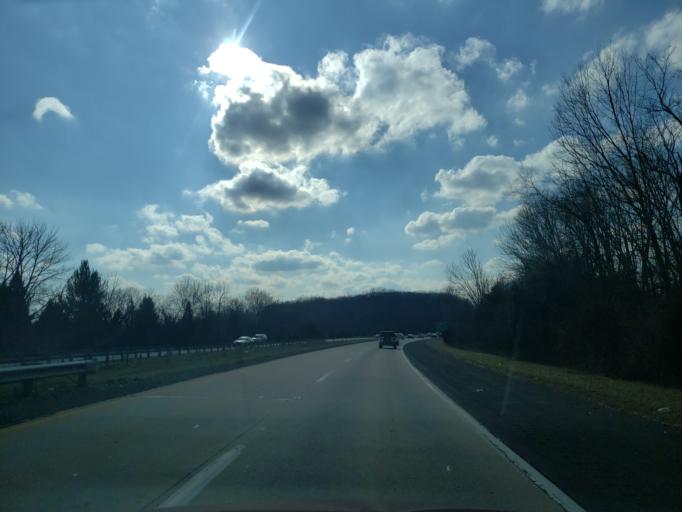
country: US
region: Pennsylvania
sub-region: Bucks County
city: Doylestown
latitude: 40.3019
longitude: -75.1193
